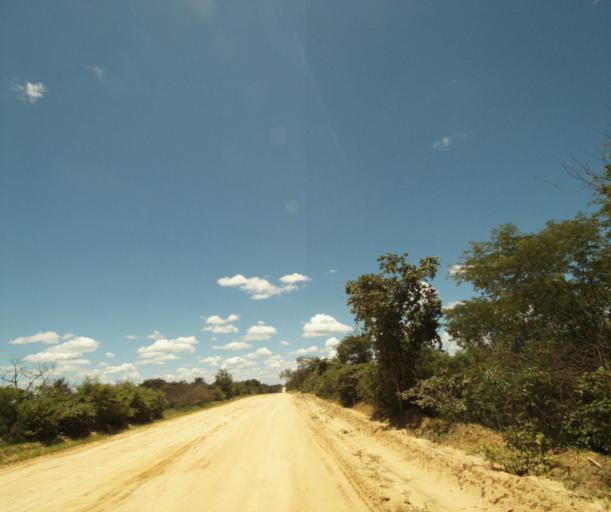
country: BR
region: Bahia
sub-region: Carinhanha
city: Carinhanha
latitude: -14.2392
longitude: -43.8526
